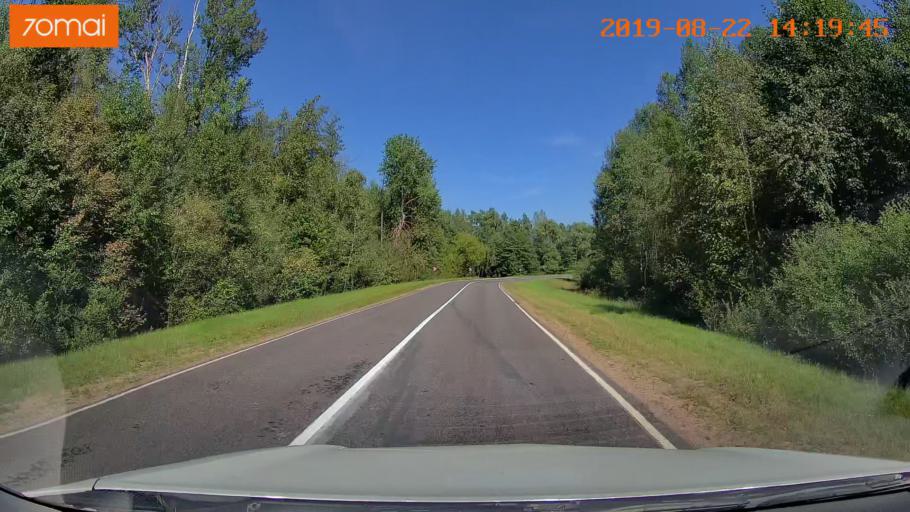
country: BY
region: Mogilev
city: Asipovichy
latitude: 53.2627
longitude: 28.5097
